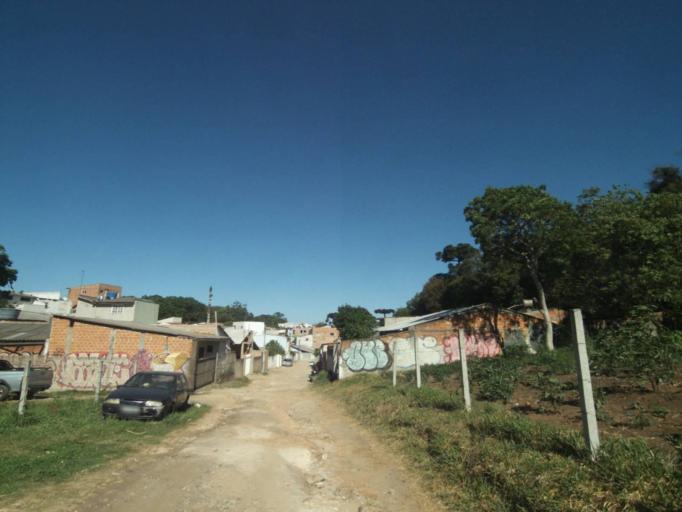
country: BR
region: Parana
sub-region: Curitiba
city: Curitiba
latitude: -25.4528
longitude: -49.3512
